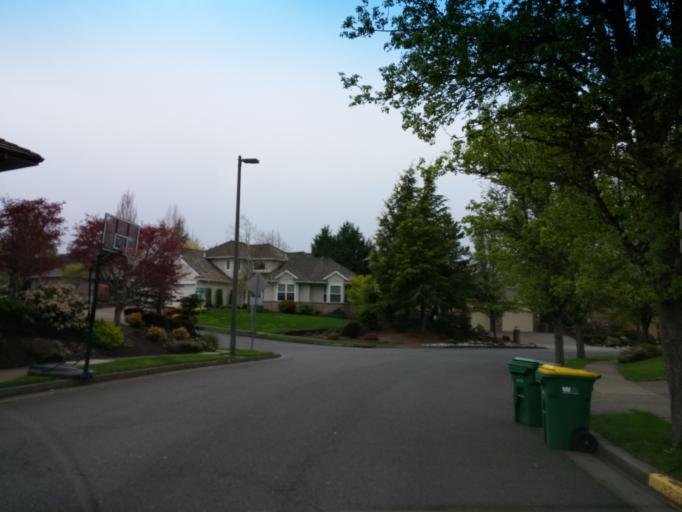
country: US
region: Oregon
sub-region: Washington County
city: Oak Hills
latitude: 45.5258
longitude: -122.8467
